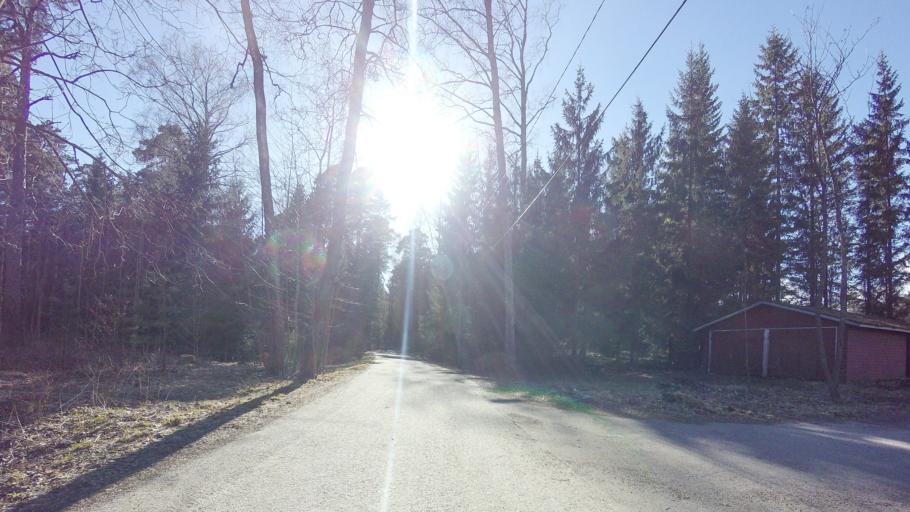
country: FI
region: Uusimaa
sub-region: Helsinki
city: Vantaa
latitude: 60.1791
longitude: 25.0659
